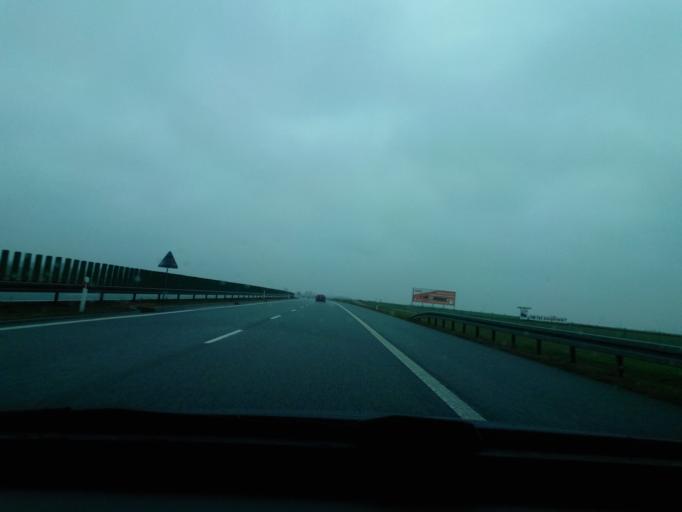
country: PL
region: Pomeranian Voivodeship
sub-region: Powiat gdanski
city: Pszczolki
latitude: 54.1382
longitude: 18.6750
